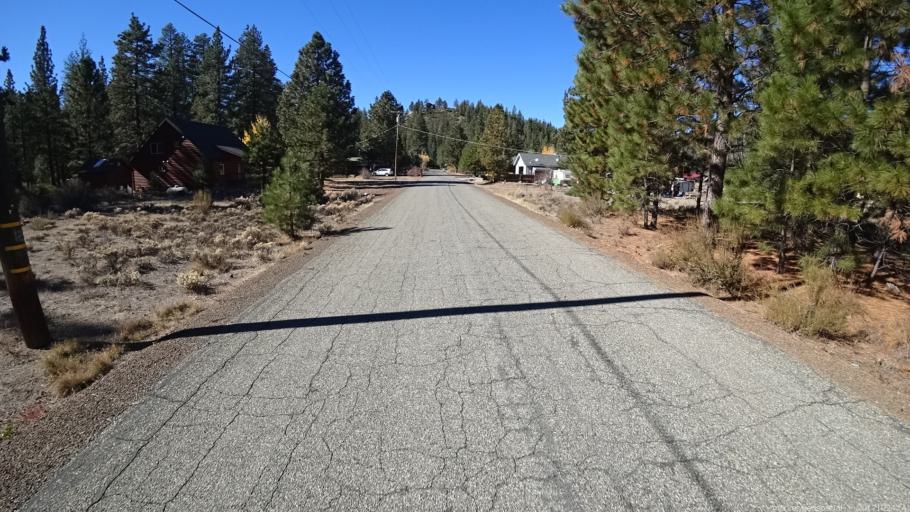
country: US
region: California
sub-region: Shasta County
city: Burney
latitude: 40.6717
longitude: -121.4295
